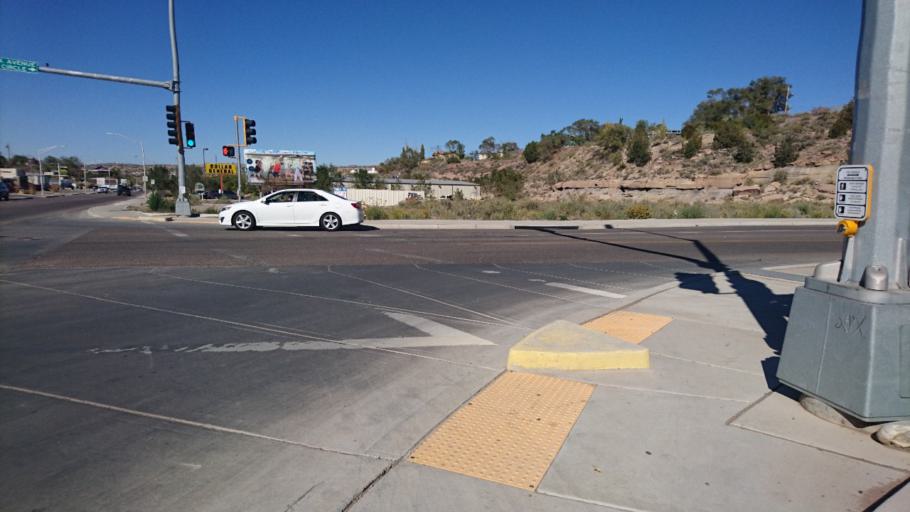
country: US
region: New Mexico
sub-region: McKinley County
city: Gallup
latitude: 35.5190
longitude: -108.7396
